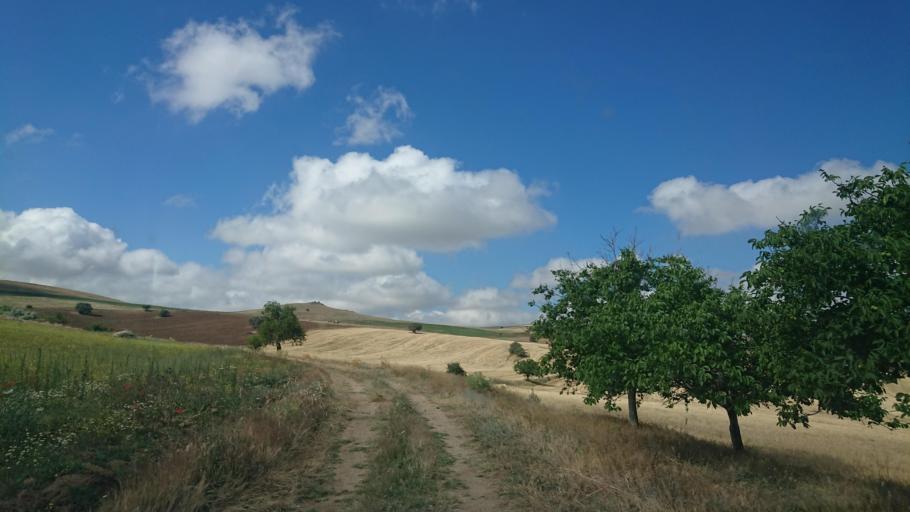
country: TR
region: Aksaray
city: Agacoren
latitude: 38.8449
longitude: 33.9366
